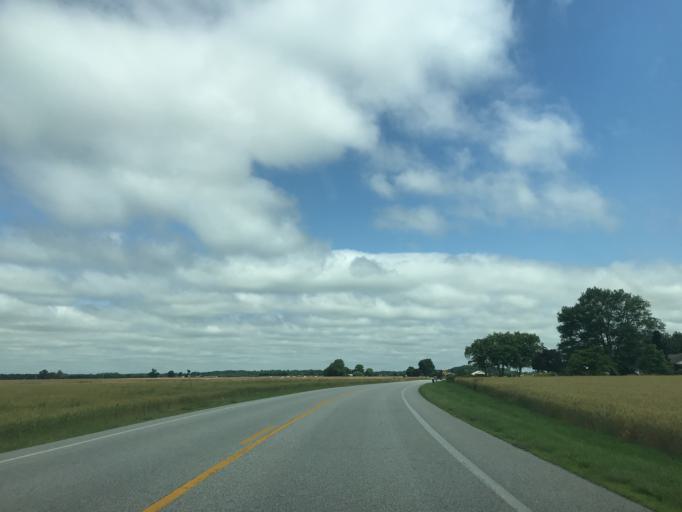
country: US
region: Maryland
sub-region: Caroline County
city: Ridgely
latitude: 38.9273
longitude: -75.8934
